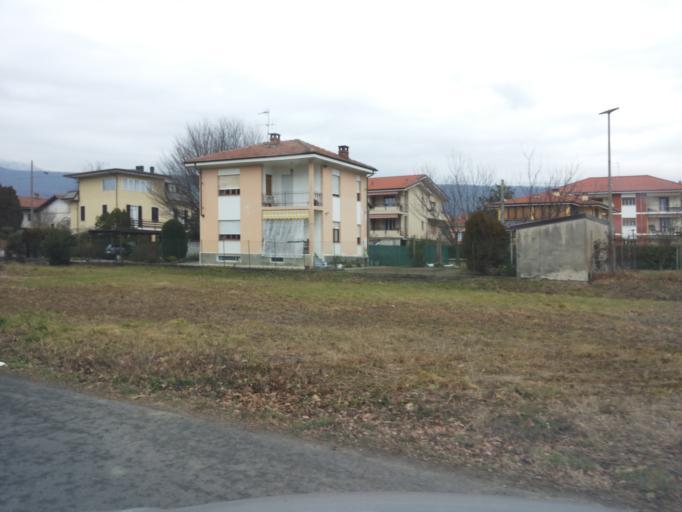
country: IT
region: Piedmont
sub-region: Provincia di Torino
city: Cascinette d'Ivrea
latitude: 45.4756
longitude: 7.9018
